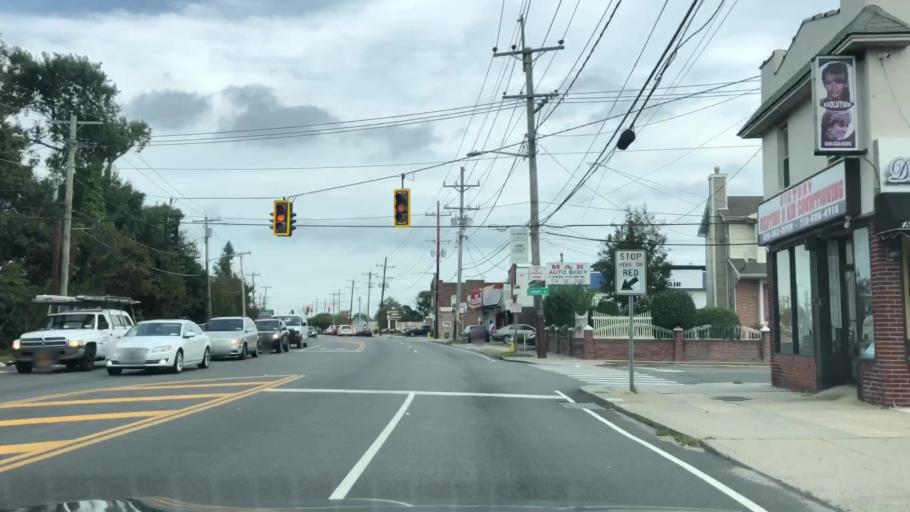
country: US
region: New York
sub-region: Nassau County
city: South Floral Park
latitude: 40.7069
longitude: -73.6966
